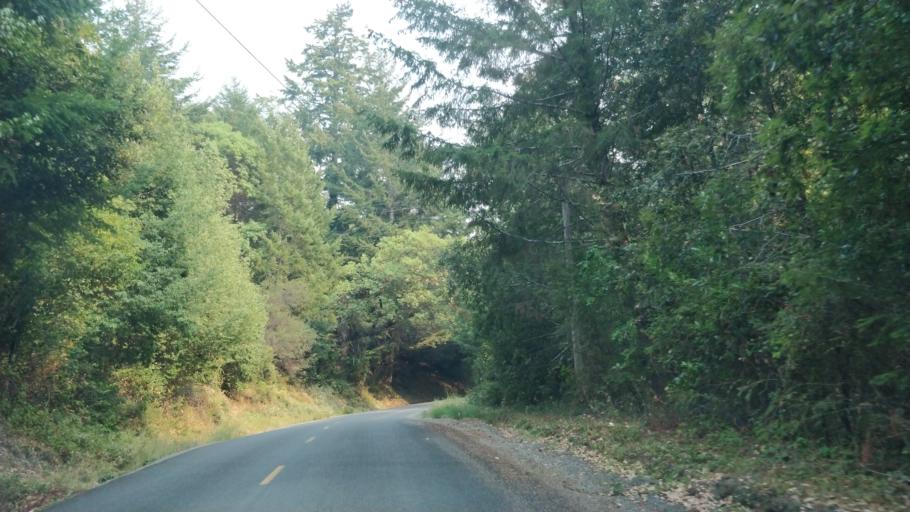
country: US
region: California
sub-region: Humboldt County
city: Rio Dell
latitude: 40.2700
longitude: -124.2123
